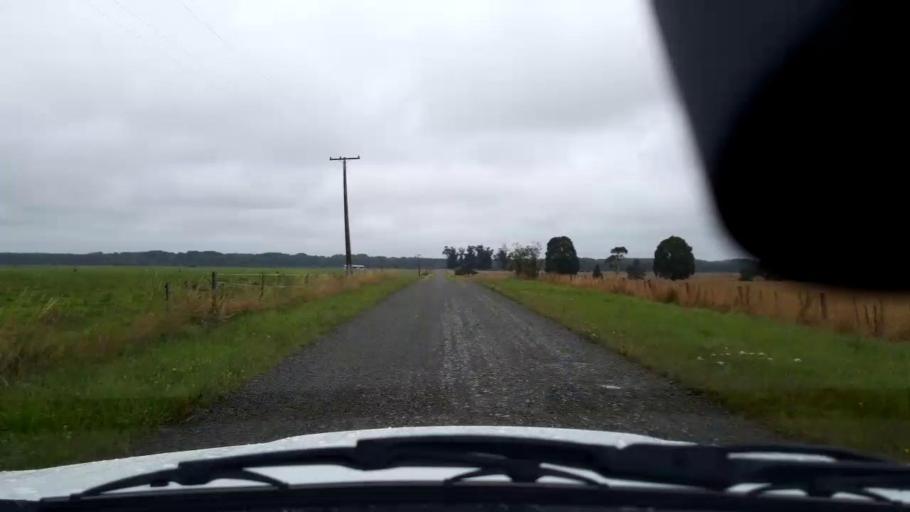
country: NZ
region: Canterbury
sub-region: Timaru District
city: Pleasant Point
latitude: -44.2453
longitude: 171.2010
